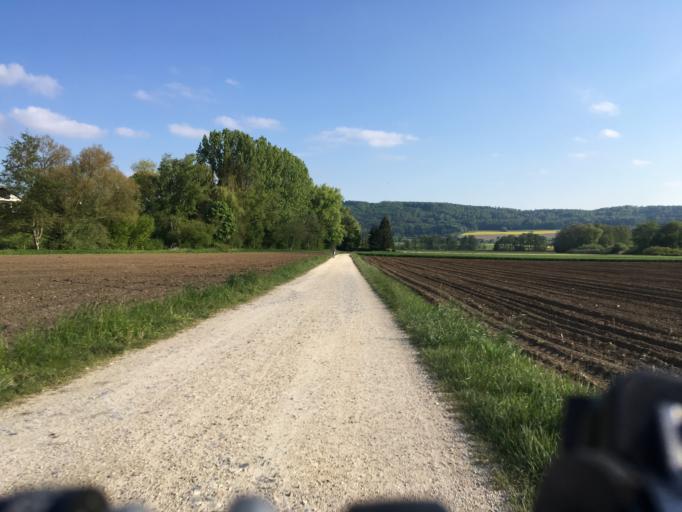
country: DE
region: Baden-Wuerttemberg
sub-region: Freiburg Region
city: Gottmadingen
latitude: 47.7287
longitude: 8.7708
